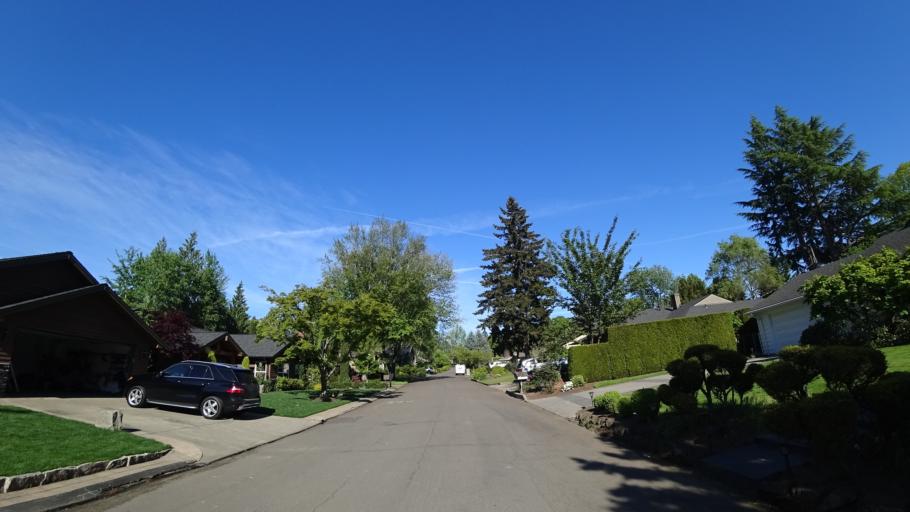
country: US
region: Oregon
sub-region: Washington County
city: Raleigh Hills
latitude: 45.4892
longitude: -122.7592
